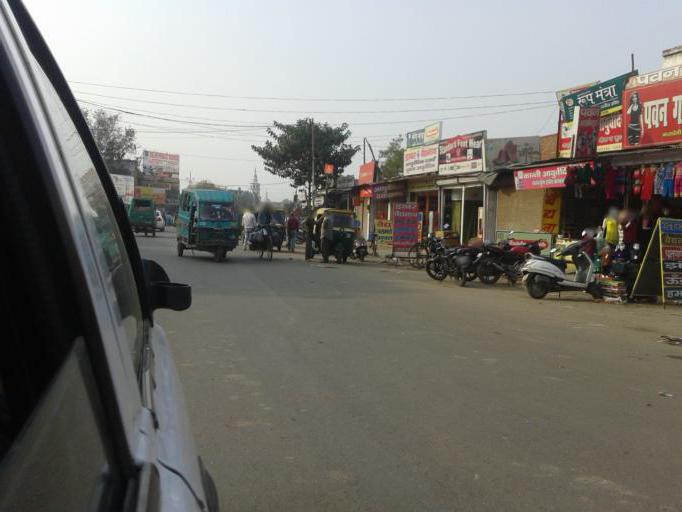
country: IN
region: Uttar Pradesh
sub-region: Kanpur
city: Kanpur
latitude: 26.4396
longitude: 80.3249
